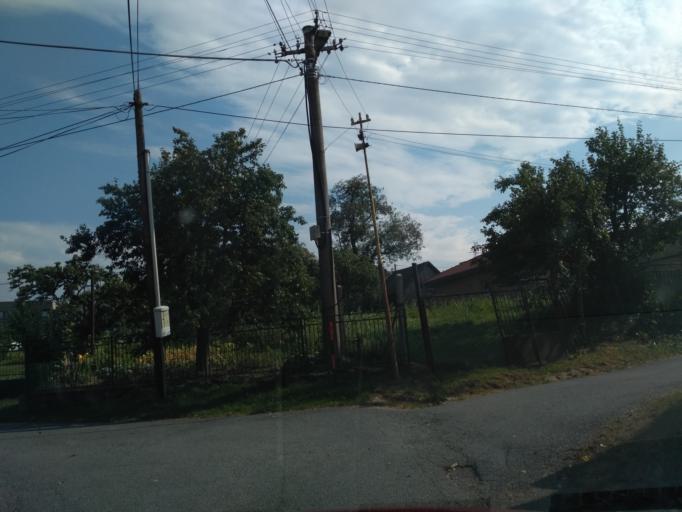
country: SK
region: Kosicky
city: Kosice
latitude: 48.8479
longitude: 21.2663
